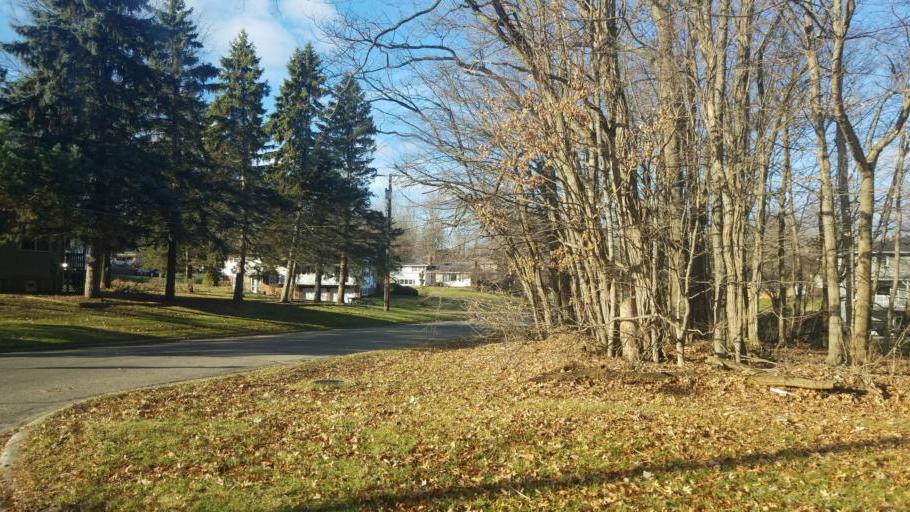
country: US
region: Ohio
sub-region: Richland County
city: Ontario
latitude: 40.7553
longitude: -82.5966
